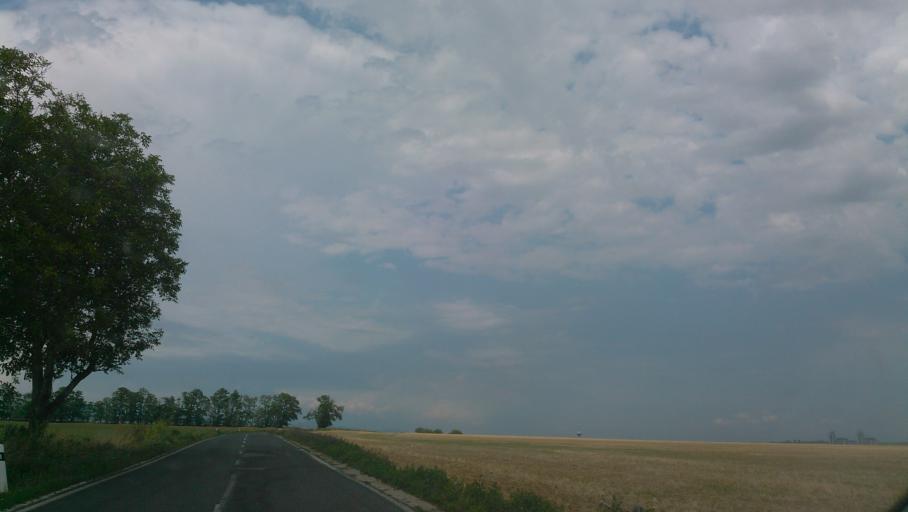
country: SK
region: Trnavsky
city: Hlohovec
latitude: 48.4810
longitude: 17.9668
